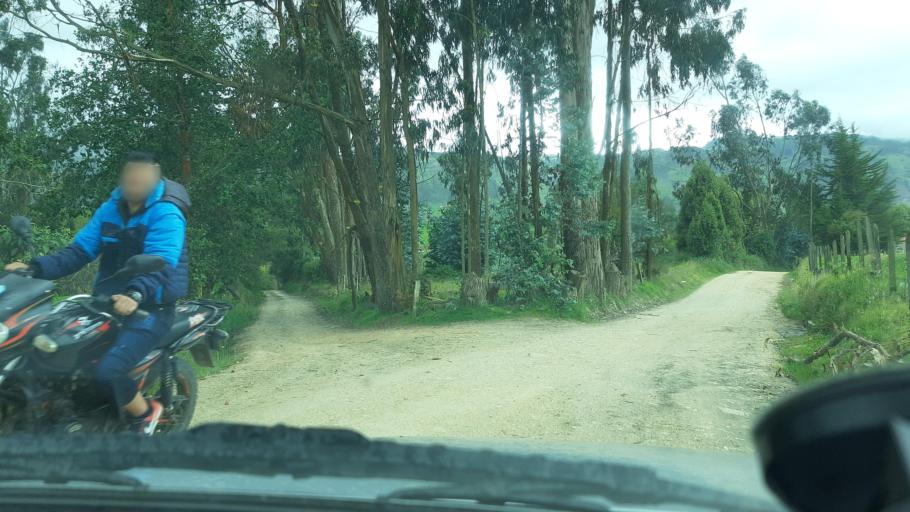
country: CO
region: Cundinamarca
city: Umbita
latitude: 5.2452
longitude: -73.4671
